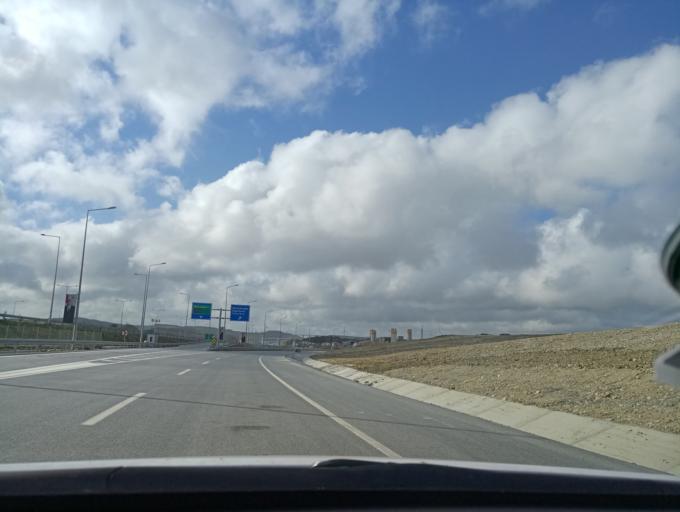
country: TR
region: Istanbul
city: Durusu
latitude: 41.2440
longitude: 28.7362
